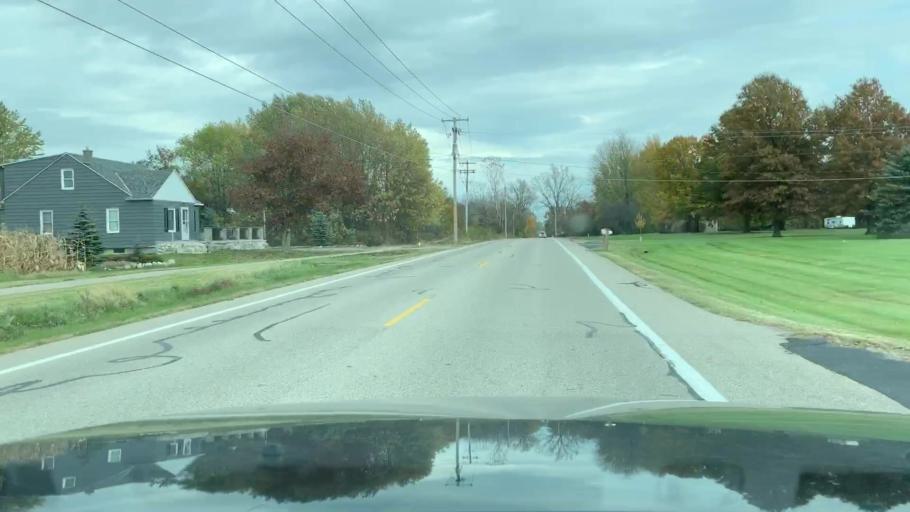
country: US
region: Michigan
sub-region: Ottawa County
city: Holland
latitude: 42.7760
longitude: -86.0684
